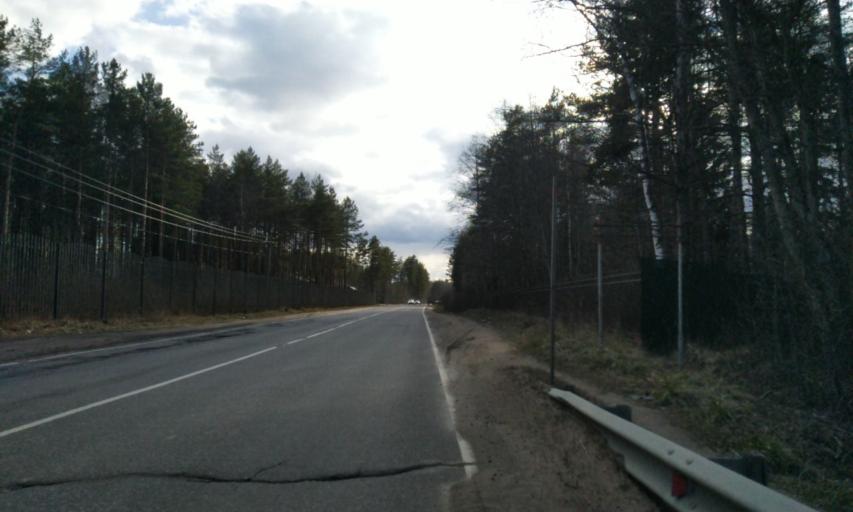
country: RU
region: Leningrad
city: Toksovo
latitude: 60.1247
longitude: 30.4584
